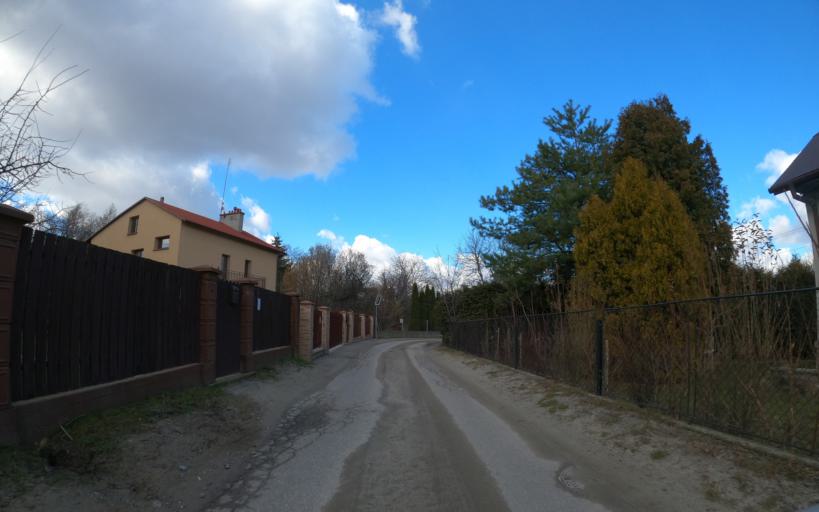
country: PL
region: Subcarpathian Voivodeship
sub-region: Powiat debicki
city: Debica
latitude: 50.0372
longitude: 21.4346
